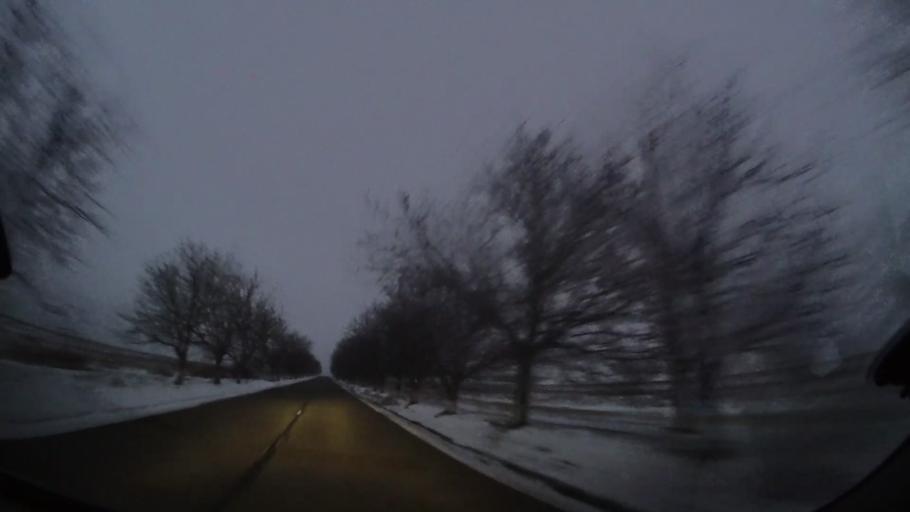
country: RO
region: Vaslui
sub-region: Comuna Hoceni
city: Hoceni
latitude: 46.5198
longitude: 28.0275
